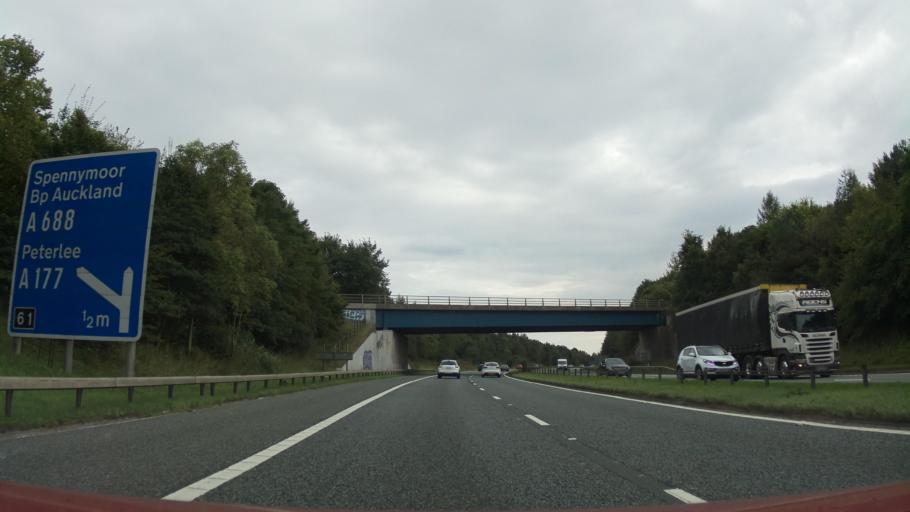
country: GB
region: England
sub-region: County Durham
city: Coxhoe
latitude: 54.7426
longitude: -1.5154
